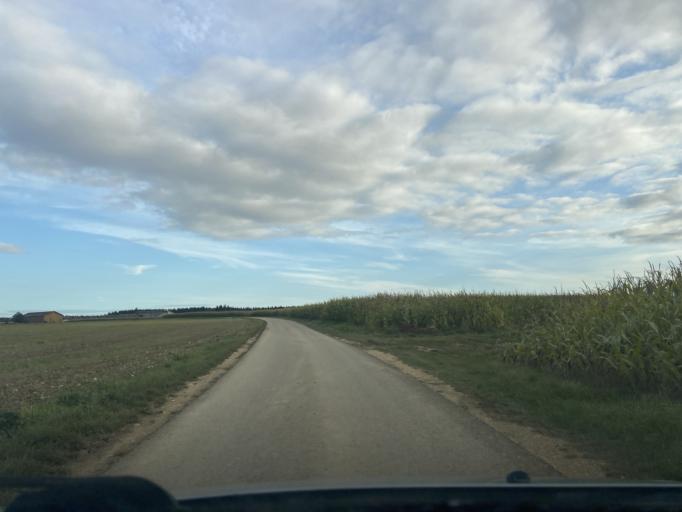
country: DE
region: Baden-Wuerttemberg
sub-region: Tuebingen Region
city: Bingen
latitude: 48.1048
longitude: 9.2646
